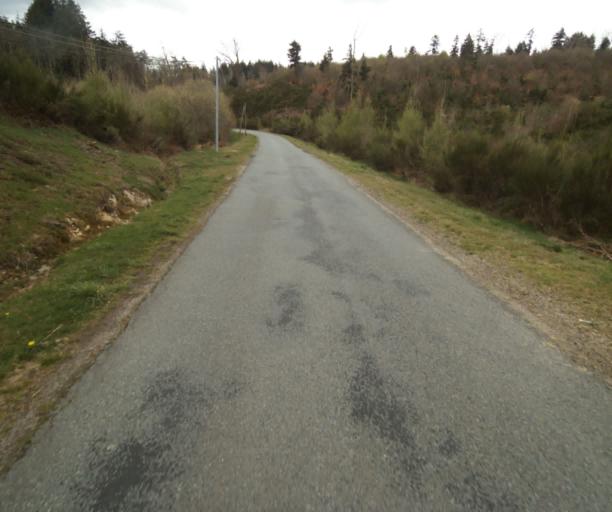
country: FR
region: Limousin
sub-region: Departement de la Correze
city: Correze
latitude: 45.3185
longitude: 1.9350
